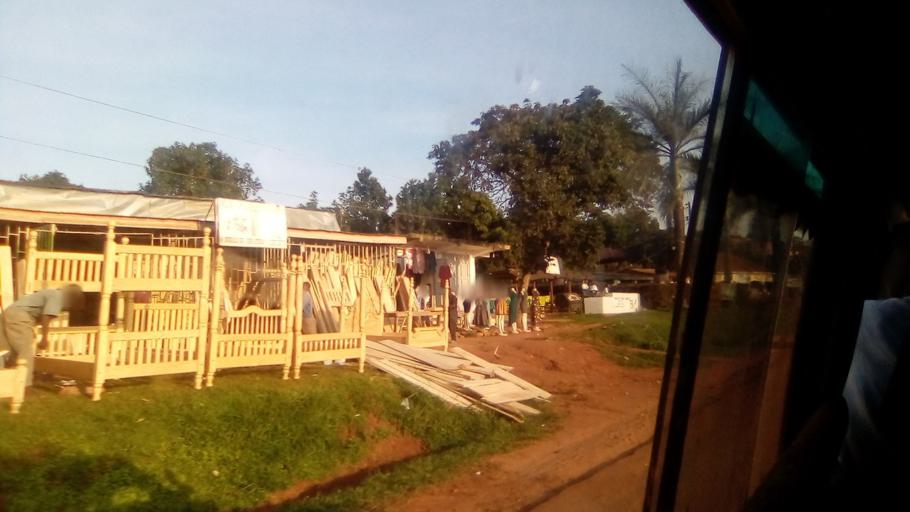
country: UG
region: Central Region
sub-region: Wakiso District
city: Kajansi
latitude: 0.1719
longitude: 32.5409
